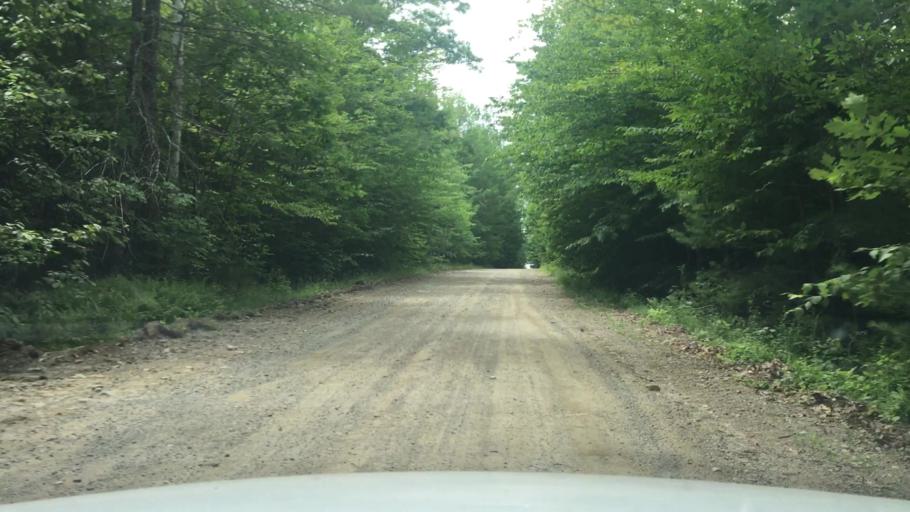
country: US
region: Maine
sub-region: Waldo County
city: Searsmont
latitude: 44.4089
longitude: -69.2703
